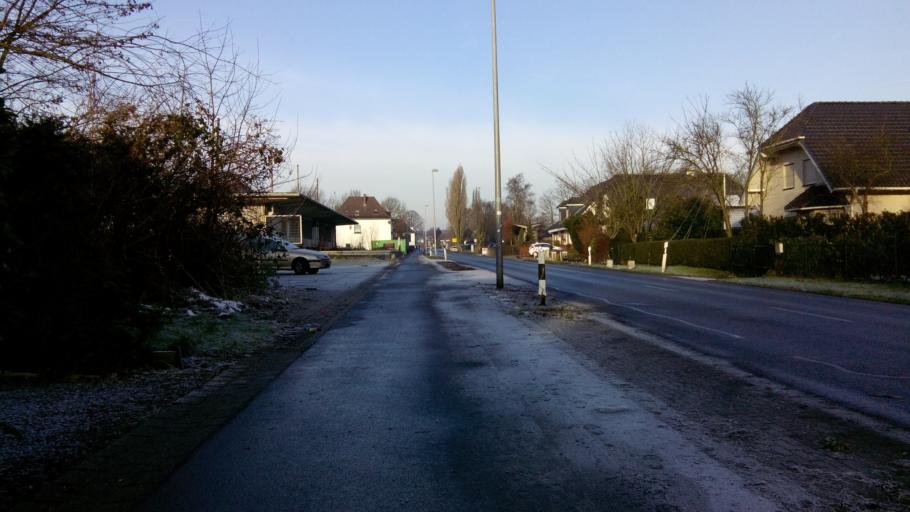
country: NL
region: Gelderland
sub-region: Gemeente Groesbeek
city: De Horst
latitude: 51.8029
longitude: 5.9702
